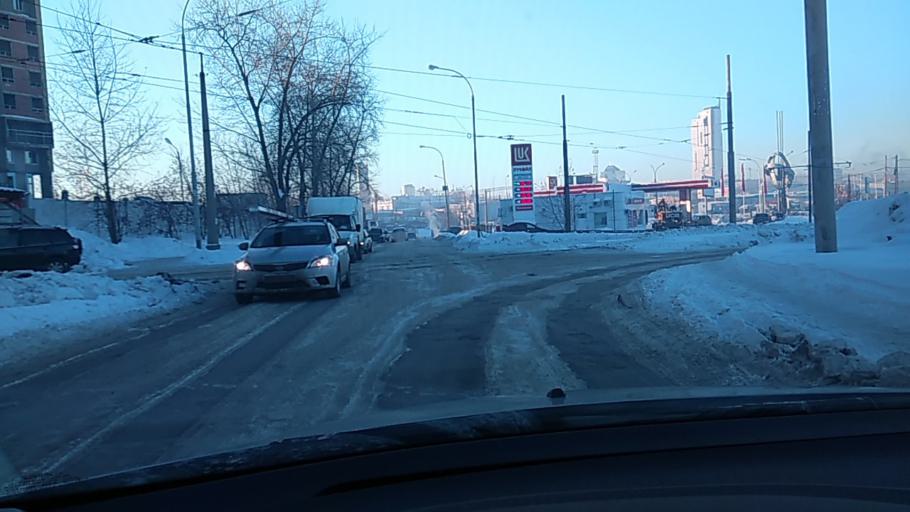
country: RU
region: Sverdlovsk
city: Yekaterinburg
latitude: 56.8611
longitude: 60.6150
